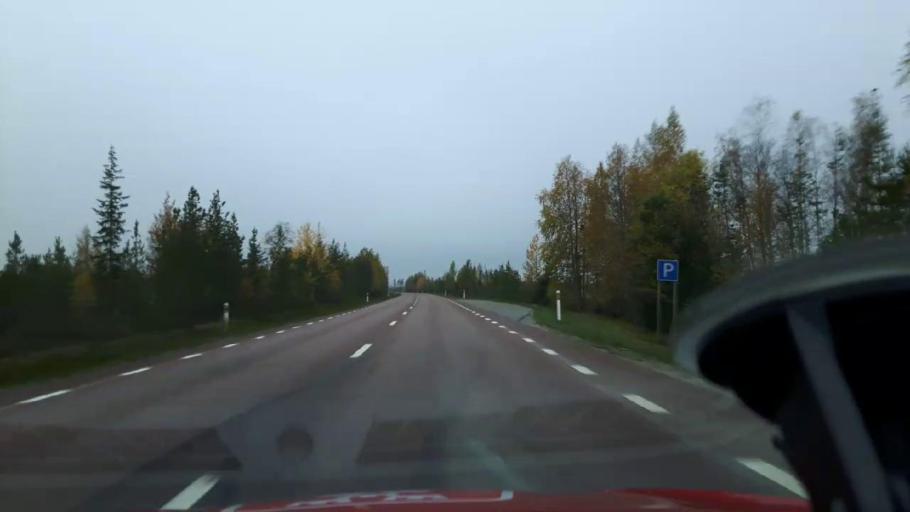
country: SE
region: Jaemtland
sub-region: Bergs Kommun
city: Hoverberg
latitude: 62.5275
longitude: 14.4468
